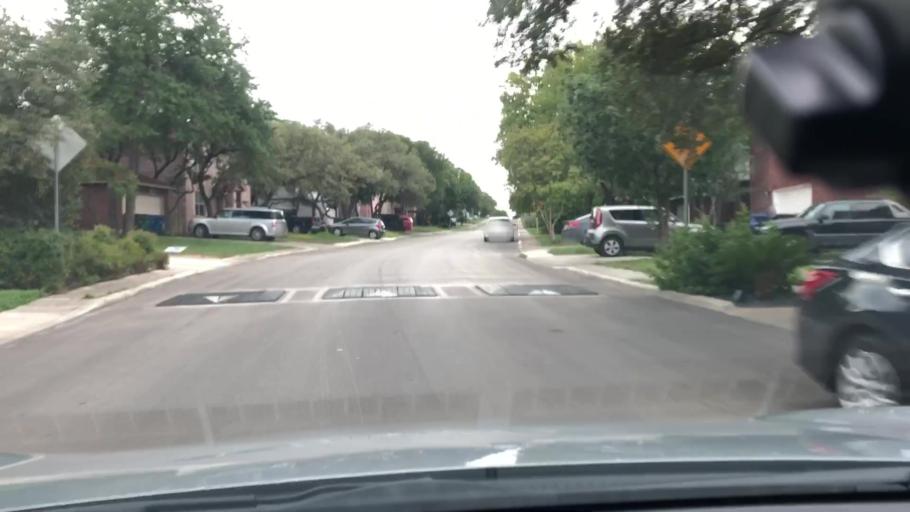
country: US
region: Texas
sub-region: Bexar County
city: Leon Valley
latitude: 29.5000
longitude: -98.6667
